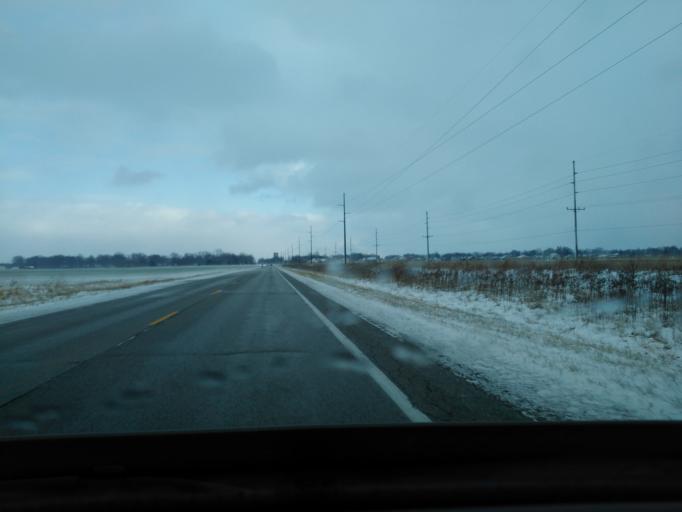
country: US
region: Illinois
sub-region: Madison County
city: Saint Jacob
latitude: 38.7177
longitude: -89.7859
